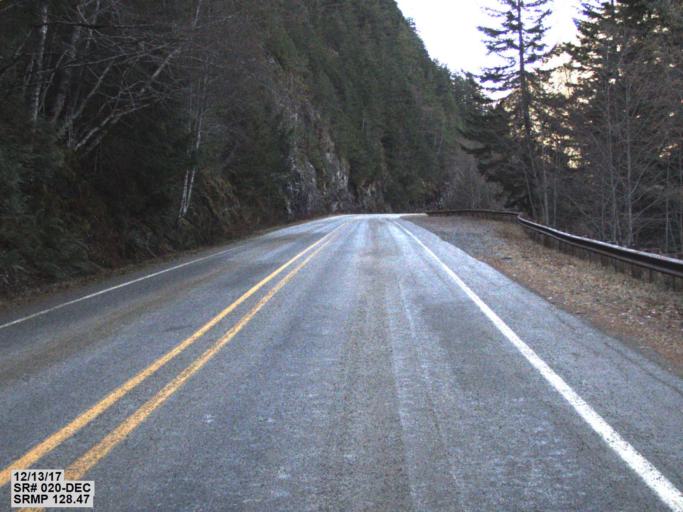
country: US
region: Washington
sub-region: Snohomish County
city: Darrington
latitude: 48.7081
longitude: -121.1169
